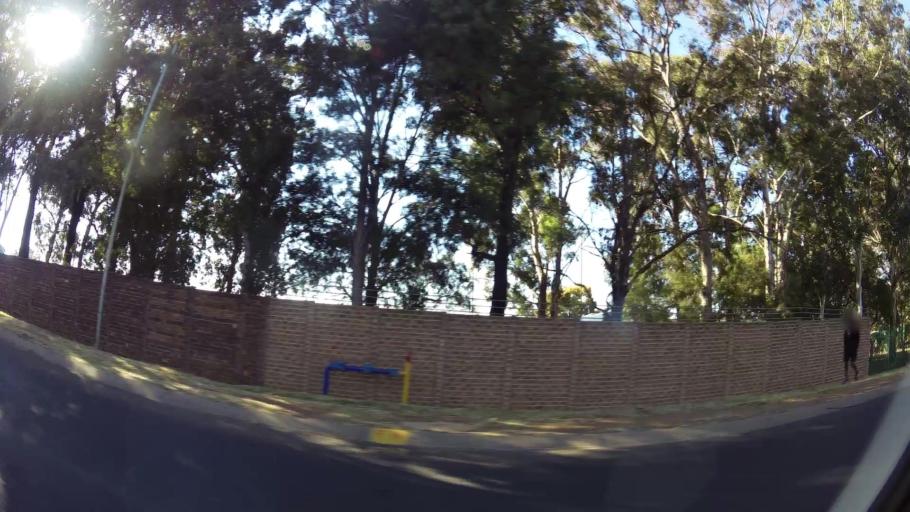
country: ZA
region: Gauteng
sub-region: Ekurhuleni Metropolitan Municipality
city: Germiston
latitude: -26.2875
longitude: 28.1204
